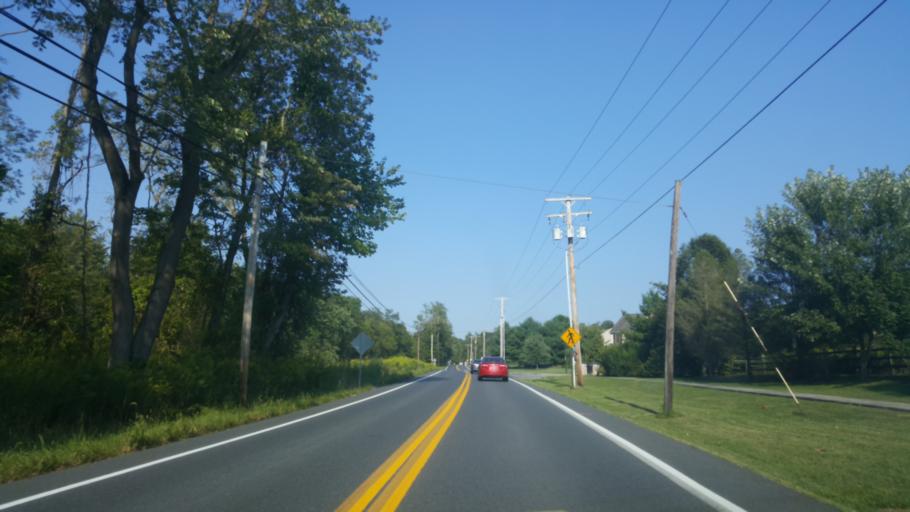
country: US
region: Pennsylvania
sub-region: Lebanon County
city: Campbelltown
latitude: 40.2388
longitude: -76.5181
